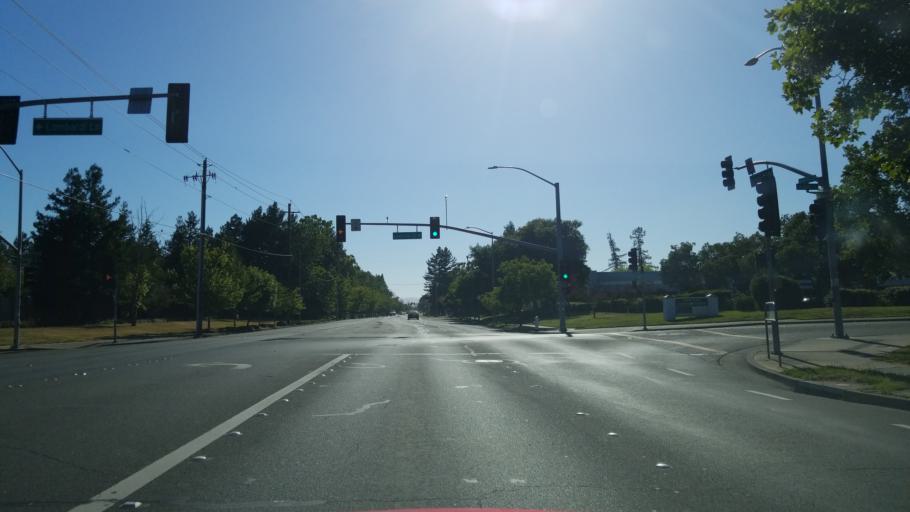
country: US
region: California
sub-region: Sonoma County
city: Roseland
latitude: 38.4264
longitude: -122.7480
